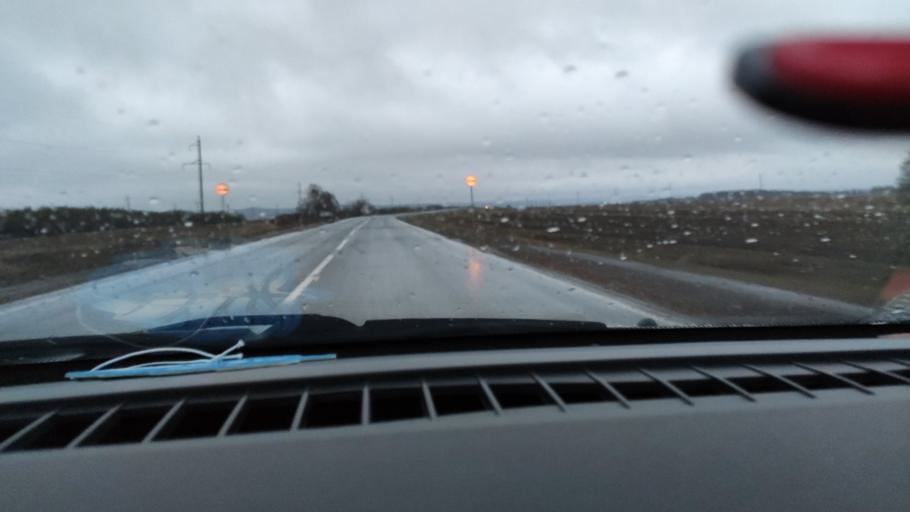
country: RU
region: Udmurtiya
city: Alnashi
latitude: 56.2019
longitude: 52.4502
